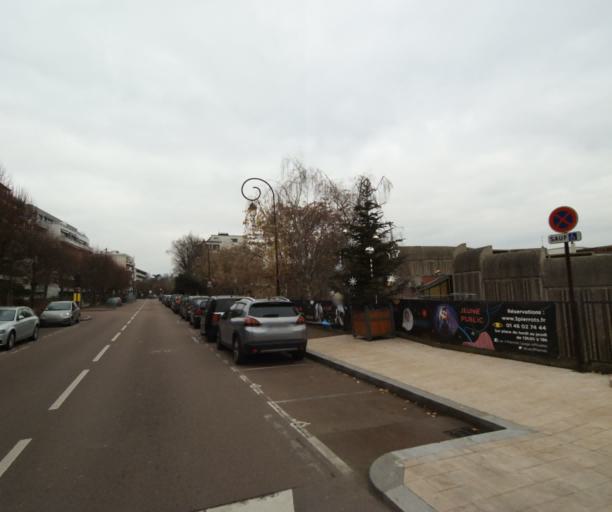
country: FR
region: Ile-de-France
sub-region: Departement des Hauts-de-Seine
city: Saint-Cloud
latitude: 48.8521
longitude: 2.2165
